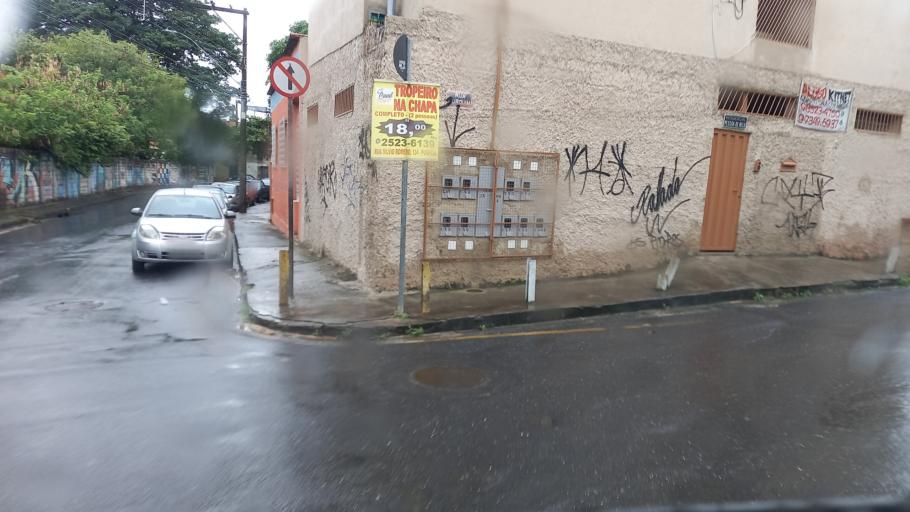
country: BR
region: Minas Gerais
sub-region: Belo Horizonte
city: Belo Horizonte
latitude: -19.9146
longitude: -43.9053
